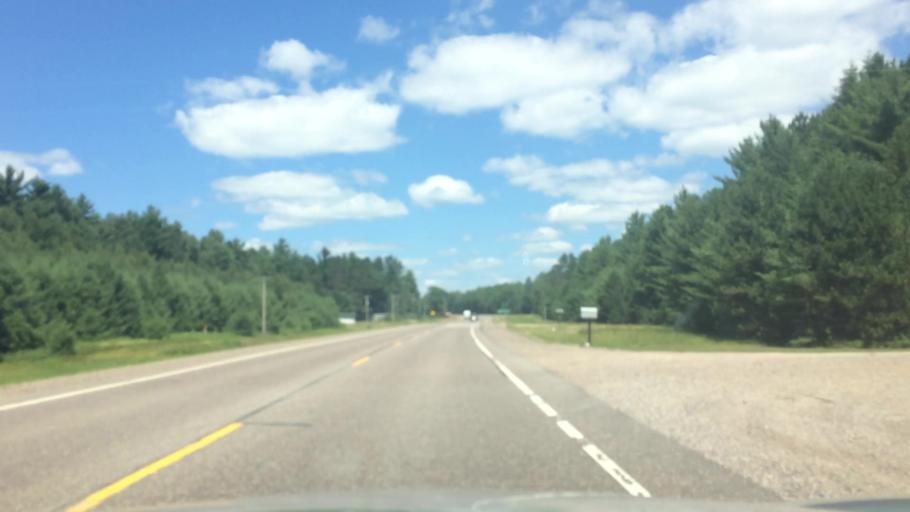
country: US
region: Wisconsin
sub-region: Vilas County
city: Lac du Flambeau
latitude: 45.9363
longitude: -89.6966
